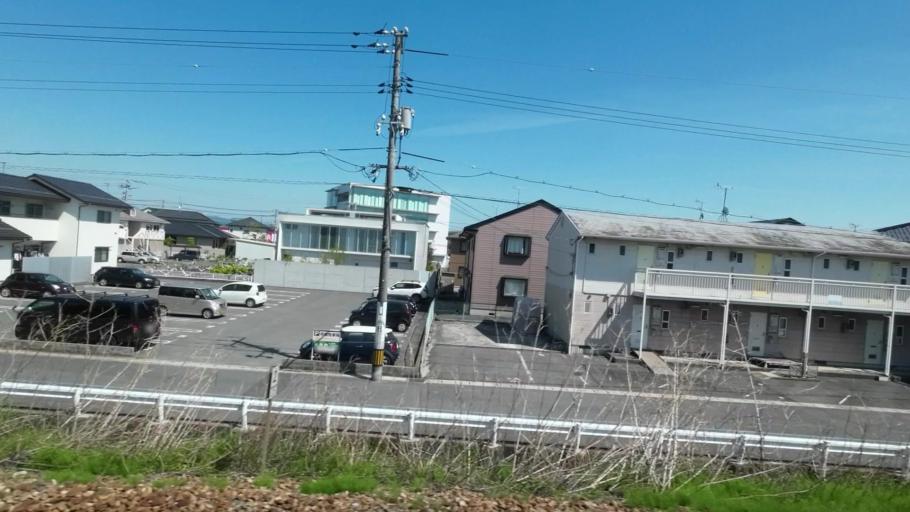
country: JP
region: Hiroshima
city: Onomichi
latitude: 34.4361
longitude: 133.2344
